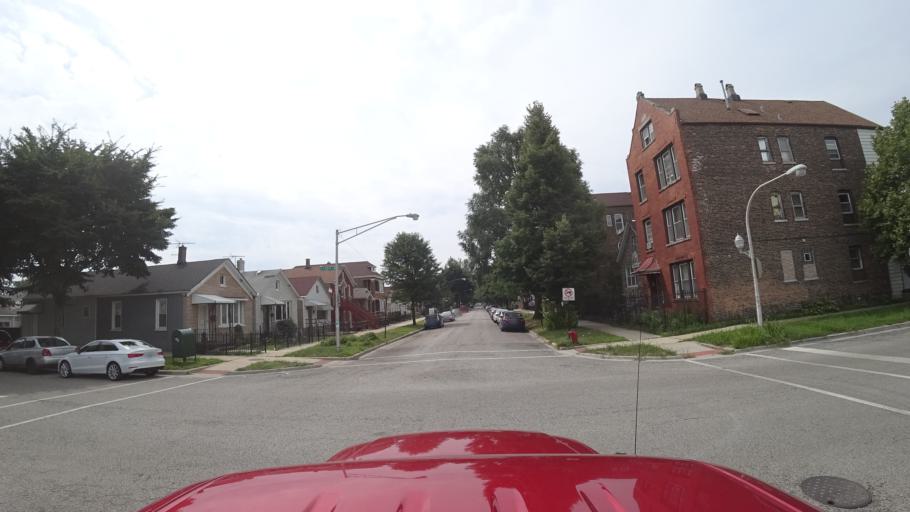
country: US
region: Illinois
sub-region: Cook County
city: Chicago
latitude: 41.8341
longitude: -87.6790
